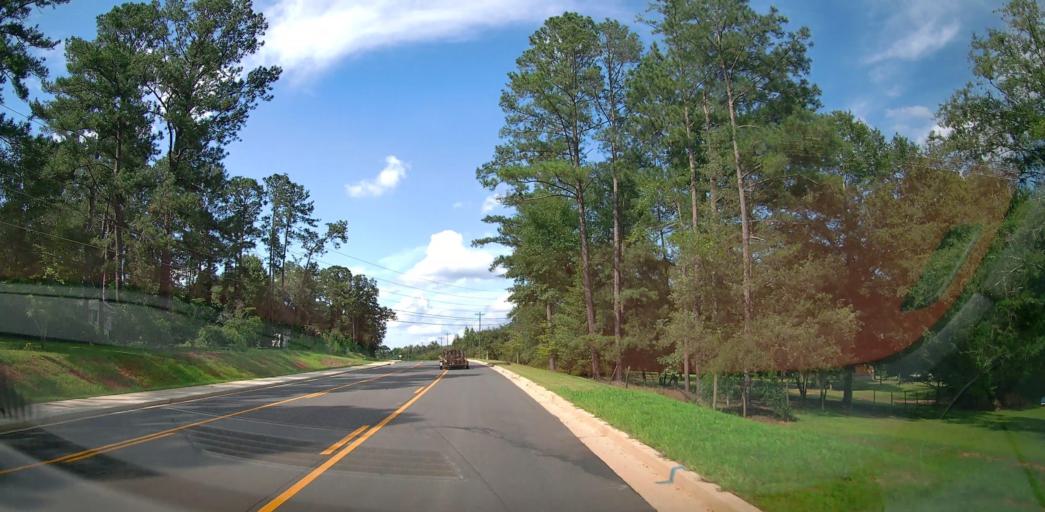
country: US
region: Georgia
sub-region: Houston County
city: Perry
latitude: 32.5046
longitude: -83.6975
